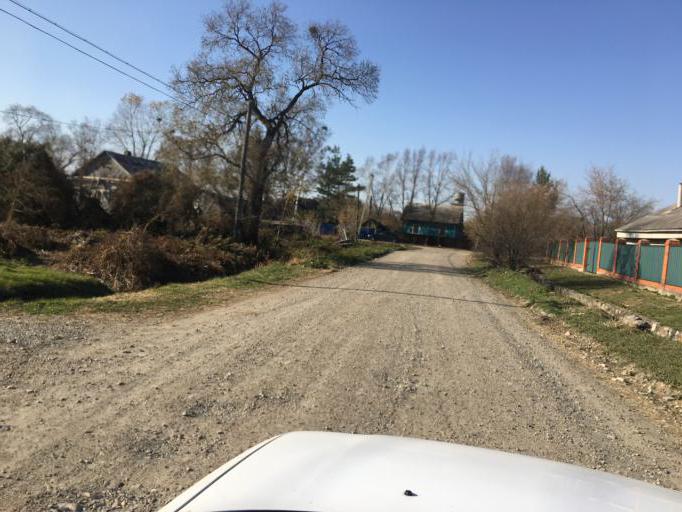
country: RU
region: Primorskiy
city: Dal'nerechensk
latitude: 45.9208
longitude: 133.7211
